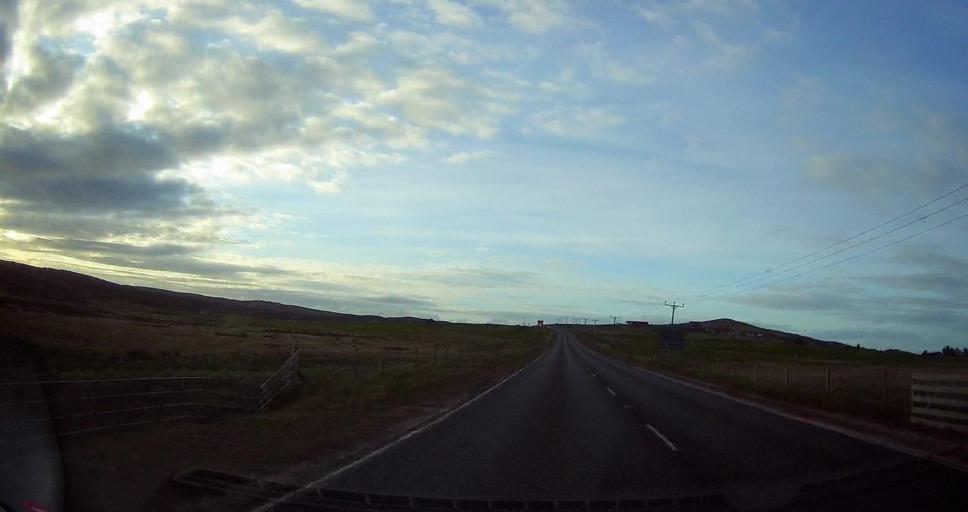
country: GB
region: Scotland
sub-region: Shetland Islands
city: Lerwick
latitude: 60.1938
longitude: -1.2320
